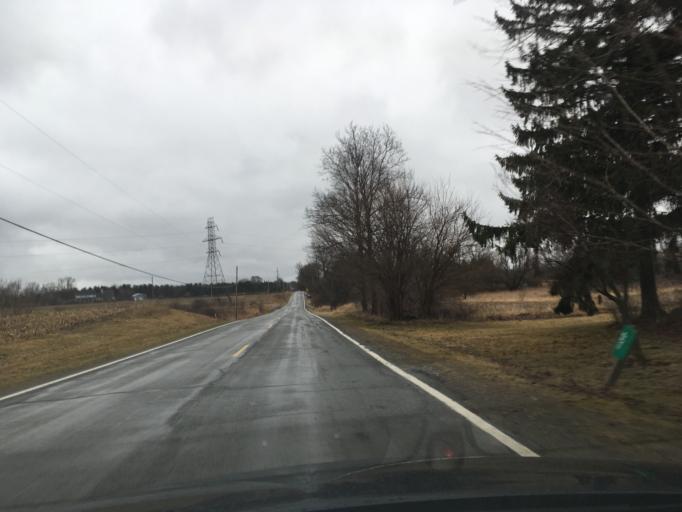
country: US
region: Michigan
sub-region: Washtenaw County
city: Chelsea
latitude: 42.2982
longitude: -84.0691
